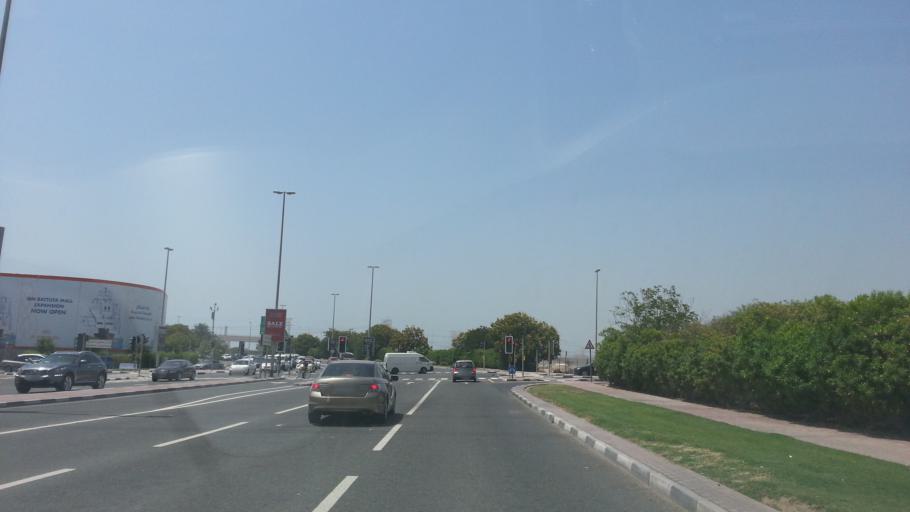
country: AE
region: Dubai
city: Dubai
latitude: 25.0505
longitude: 55.1268
